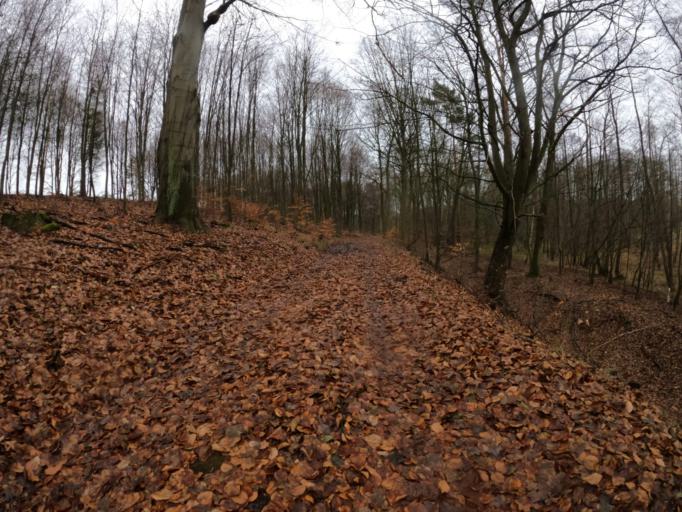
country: PL
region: West Pomeranian Voivodeship
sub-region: Powiat mysliborski
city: Debno
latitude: 52.7529
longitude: 14.7695
